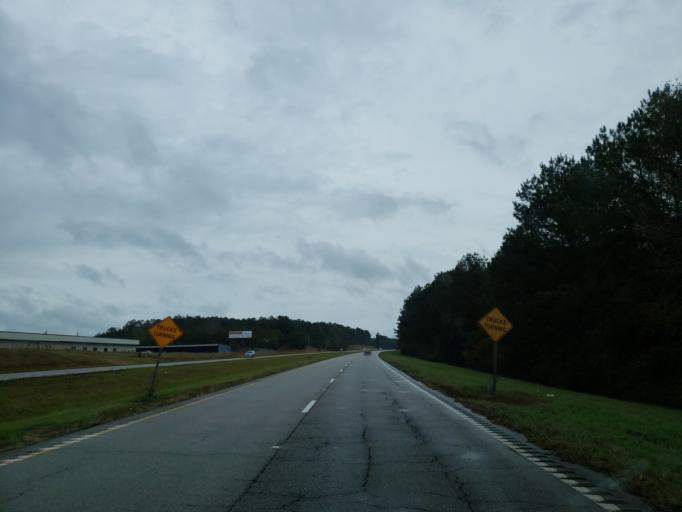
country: US
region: Mississippi
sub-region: Jones County
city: Laurel
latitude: 31.7056
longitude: -89.0708
